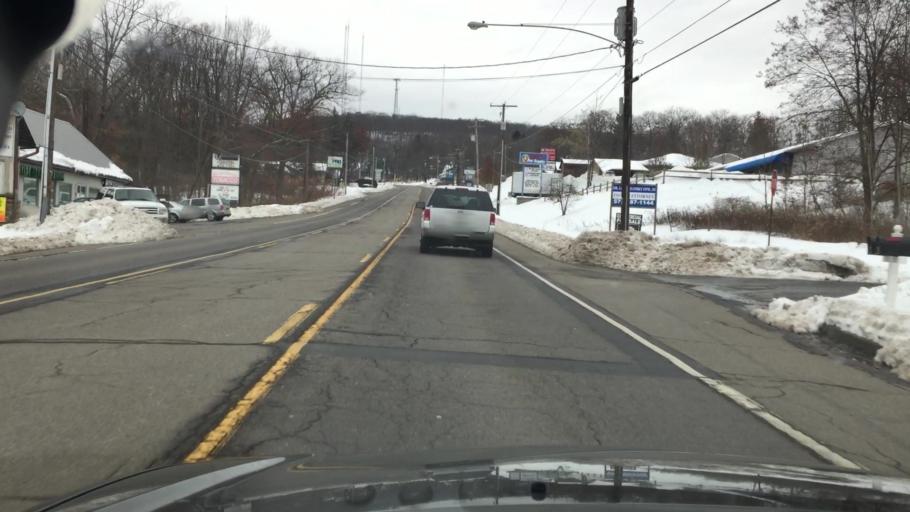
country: US
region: Pennsylvania
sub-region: Luzerne County
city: Mountain Top
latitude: 41.1667
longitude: -75.8819
